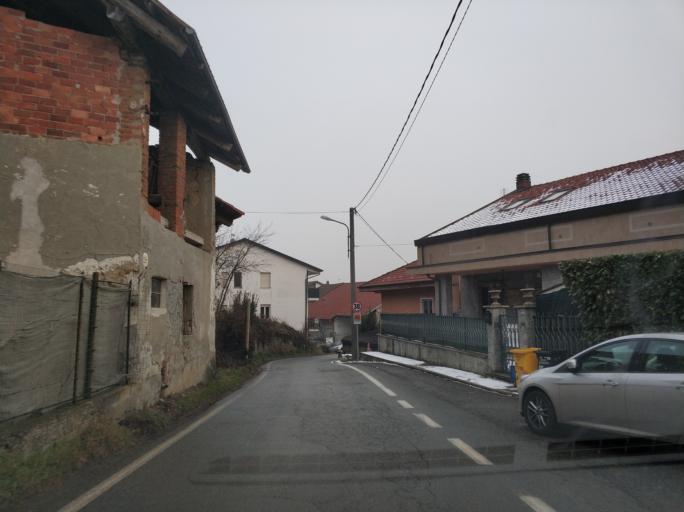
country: IT
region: Piedmont
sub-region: Provincia di Torino
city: San Francesco al Campo
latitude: 45.2202
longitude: 7.6693
